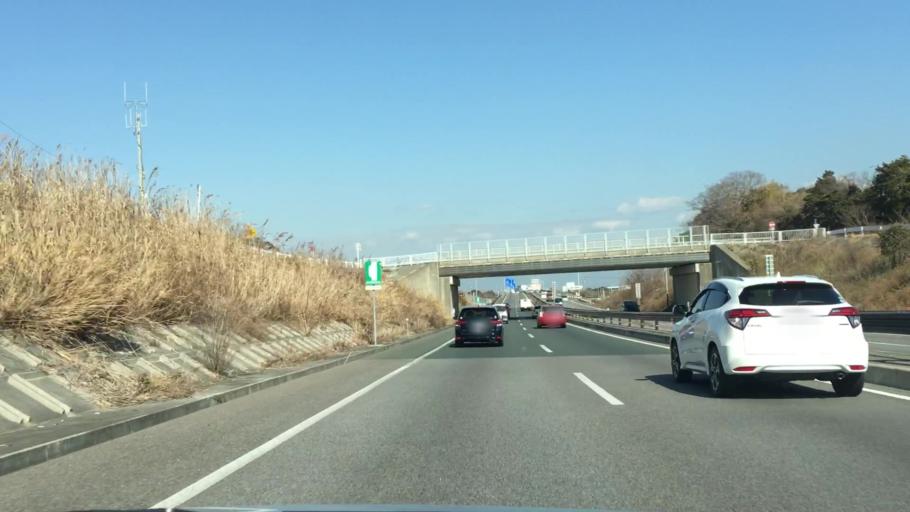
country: JP
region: Aichi
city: Toyohashi
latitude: 34.7155
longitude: 137.3524
